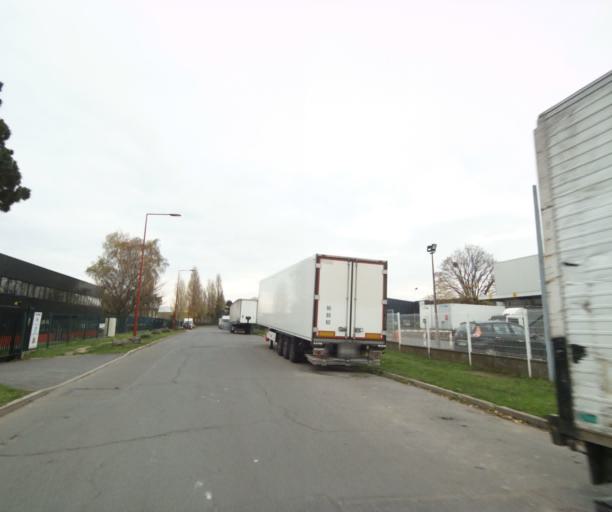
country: FR
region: Ile-de-France
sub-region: Departement du Val-d'Oise
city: Gonesse
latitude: 48.9831
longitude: 2.4626
